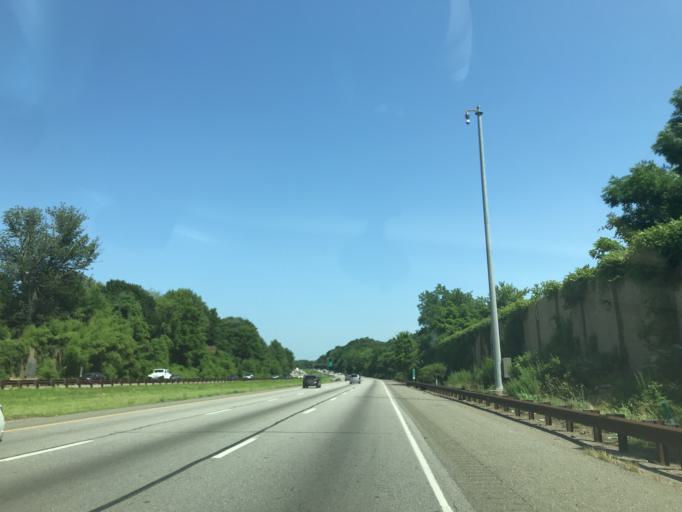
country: US
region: Pennsylvania
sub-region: Delaware County
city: Radnor
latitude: 40.0152
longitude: -75.3572
